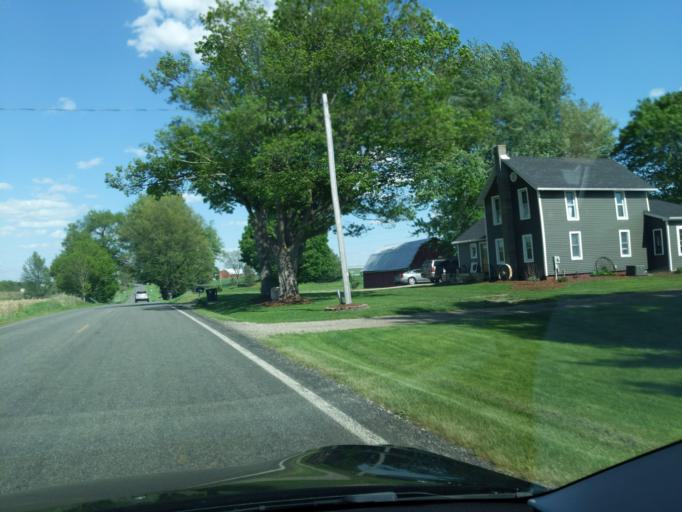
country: US
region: Michigan
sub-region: Ionia County
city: Lake Odessa
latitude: 42.7841
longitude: -85.2212
